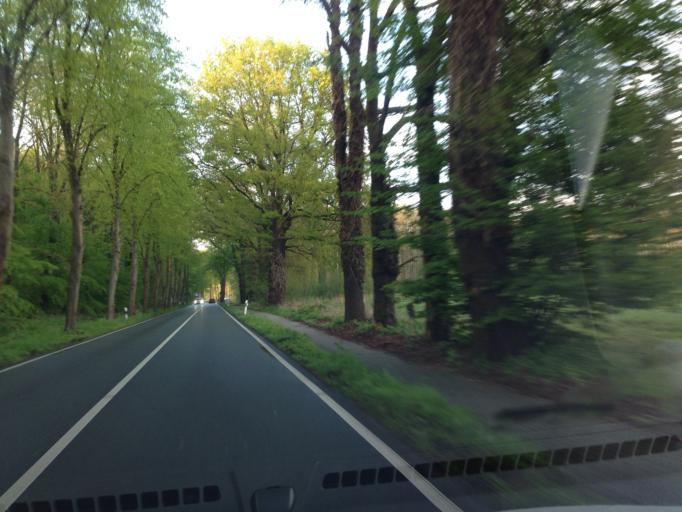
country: DE
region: North Rhine-Westphalia
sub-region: Regierungsbezirk Munster
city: Muenster
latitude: 51.9867
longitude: 7.6788
